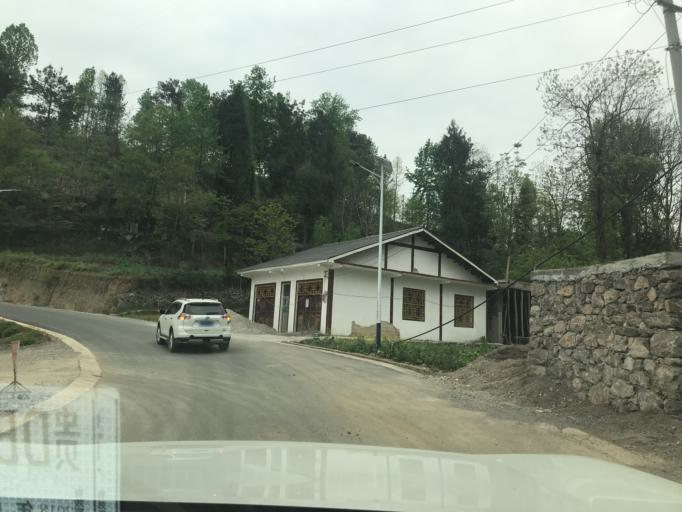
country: CN
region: Guizhou Sheng
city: Tongjing
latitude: 28.3053
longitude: 108.2718
